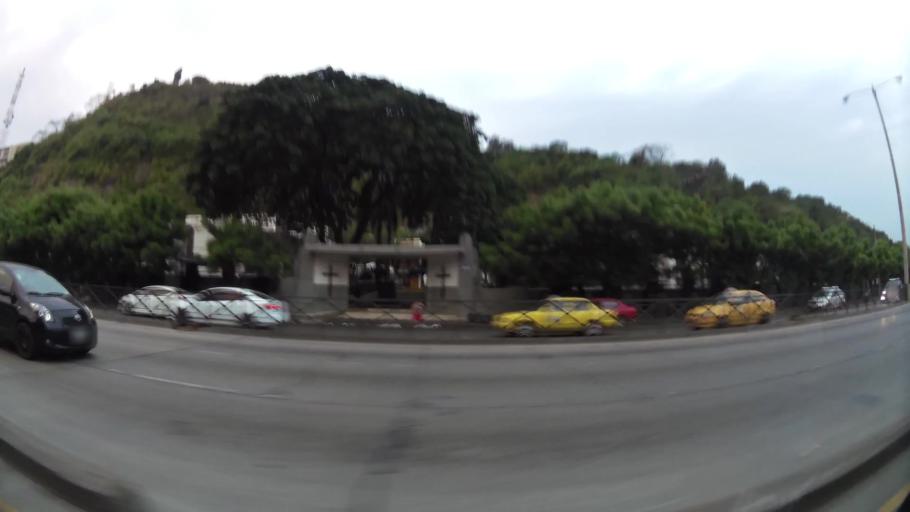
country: EC
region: Guayas
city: Eloy Alfaro
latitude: -2.1789
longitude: -79.8854
